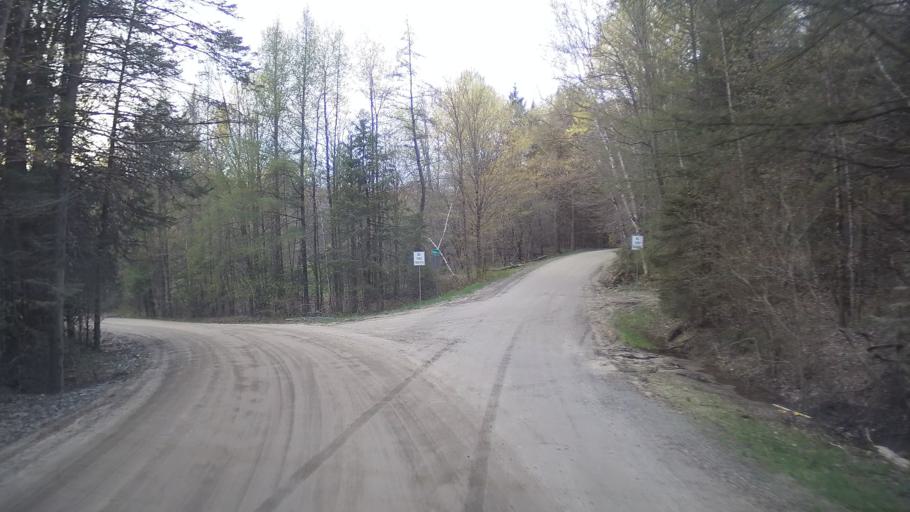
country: US
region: Vermont
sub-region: Caledonia County
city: Lyndonville
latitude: 44.6005
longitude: -71.9601
